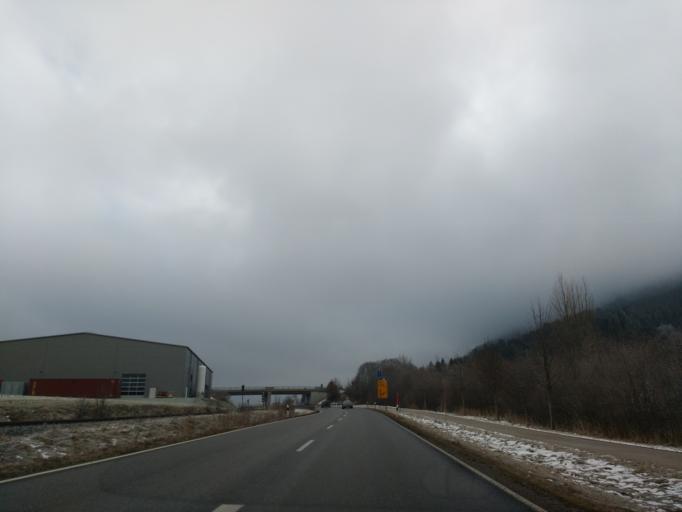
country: DE
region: Bavaria
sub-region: Swabia
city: Nesselwang
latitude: 47.6164
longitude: 10.5154
